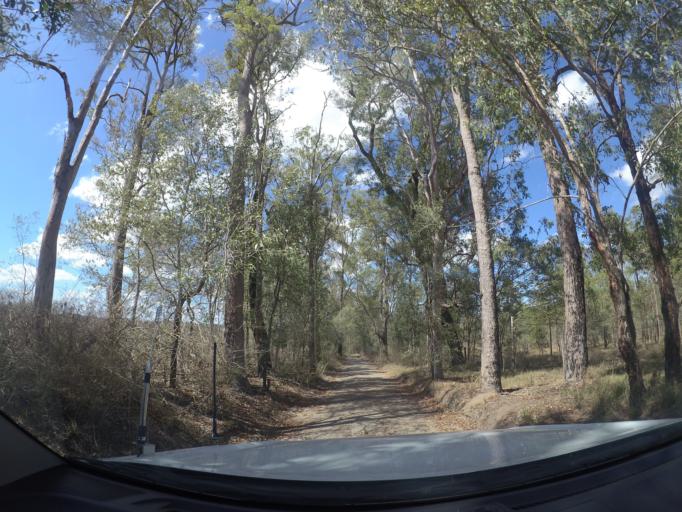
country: AU
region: Queensland
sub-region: Logan
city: Cedar Vale
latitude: -27.8406
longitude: 152.9743
